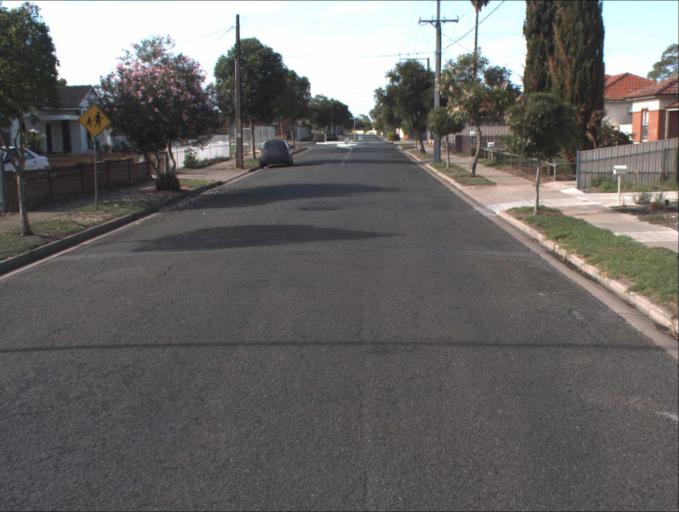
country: AU
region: South Australia
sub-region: Charles Sturt
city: Woodville North
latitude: -34.8647
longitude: 138.5512
